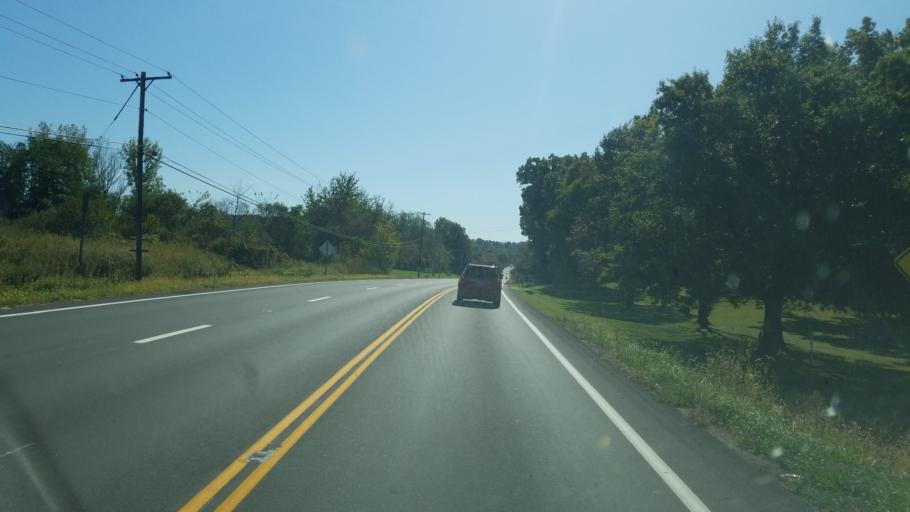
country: US
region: Ohio
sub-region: Stark County
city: Navarre
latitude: 40.7122
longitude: -81.5221
